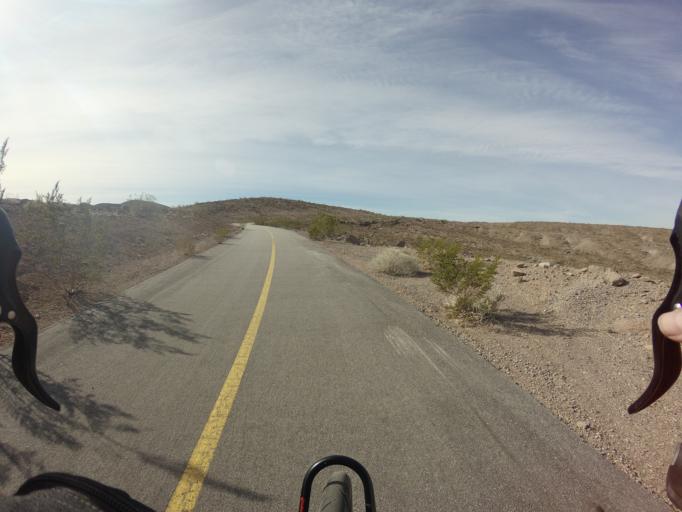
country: US
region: Nevada
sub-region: Clark County
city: Henderson
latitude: 36.1105
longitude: -114.8788
